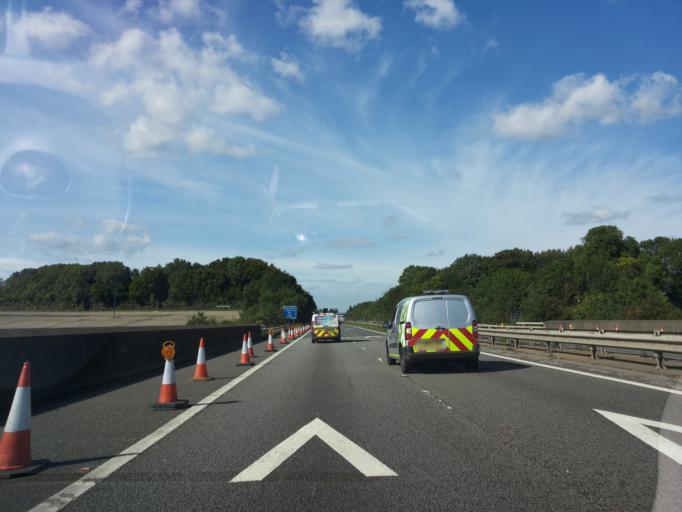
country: GB
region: England
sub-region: Kent
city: Sittingbourne
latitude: 51.3029
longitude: 0.7262
